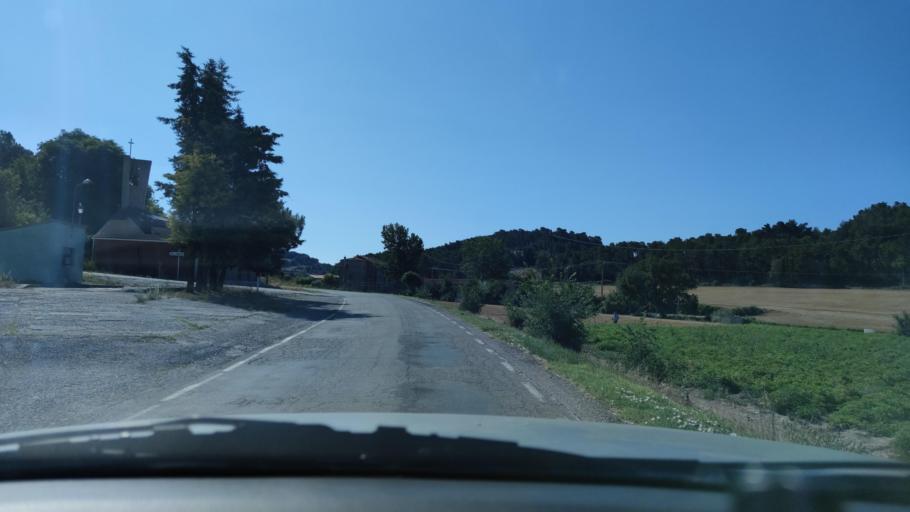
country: ES
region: Catalonia
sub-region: Provincia de Barcelona
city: Pujalt
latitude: 41.6882
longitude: 1.3887
